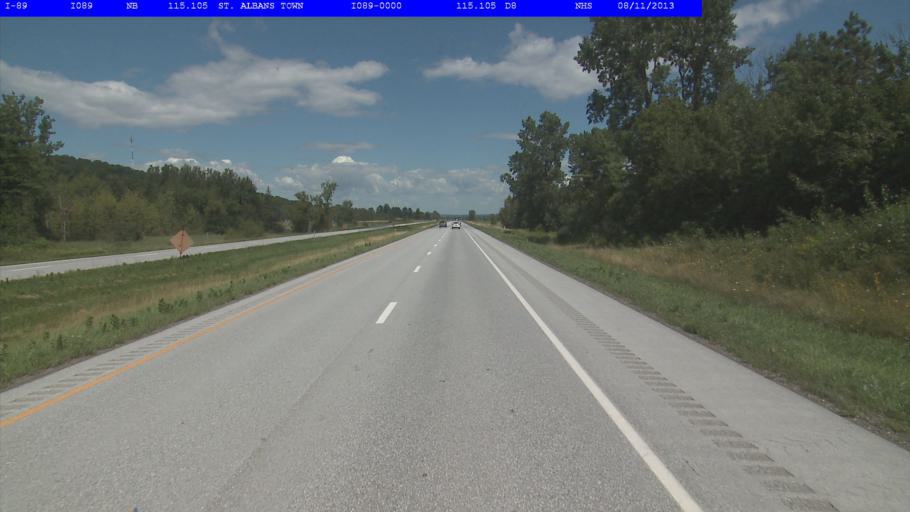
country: US
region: Vermont
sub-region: Franklin County
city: Saint Albans
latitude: 44.8139
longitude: -73.0635
